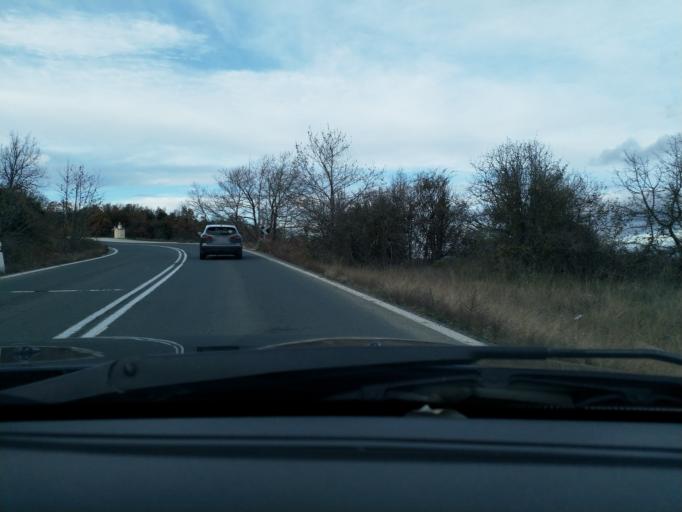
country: GR
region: Thessaly
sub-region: Trikala
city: Kastraki
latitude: 39.7480
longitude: 21.5158
